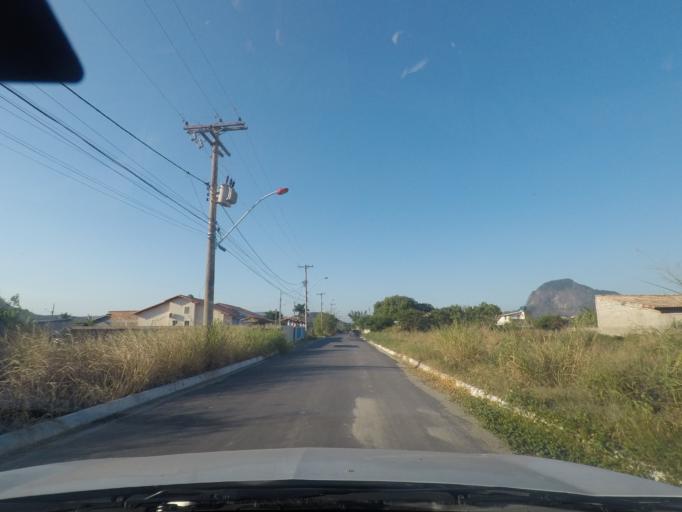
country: BR
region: Rio de Janeiro
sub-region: Marica
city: Marica
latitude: -22.9593
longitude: -42.9334
